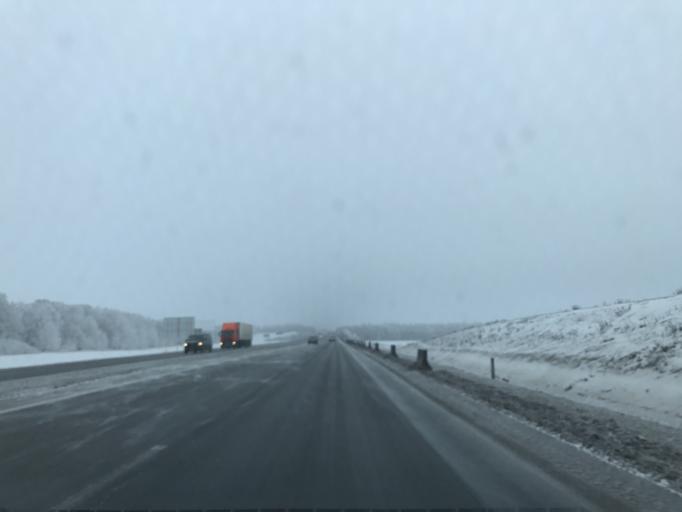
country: RU
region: Rostov
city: Grushevskaya
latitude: 47.5127
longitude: 39.9708
